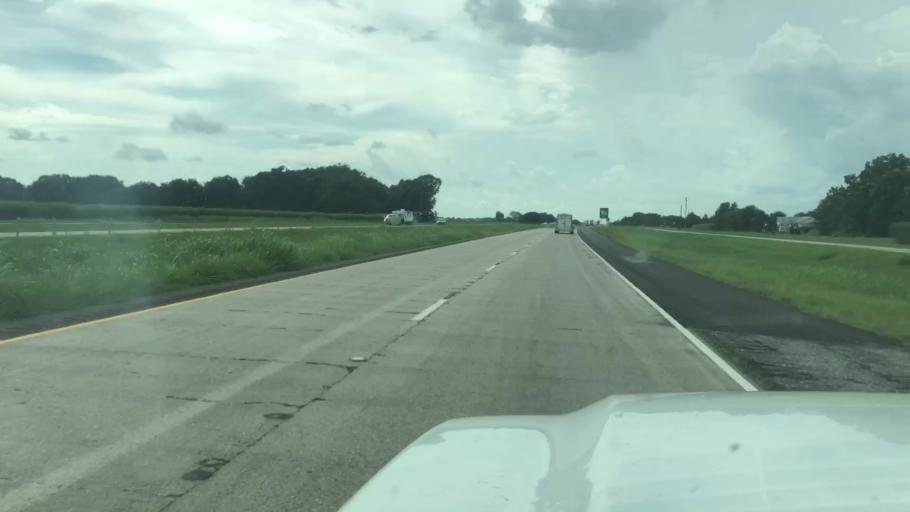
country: US
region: Louisiana
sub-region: Iberia Parish
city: Jeanerette
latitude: 29.8618
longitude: -91.6236
